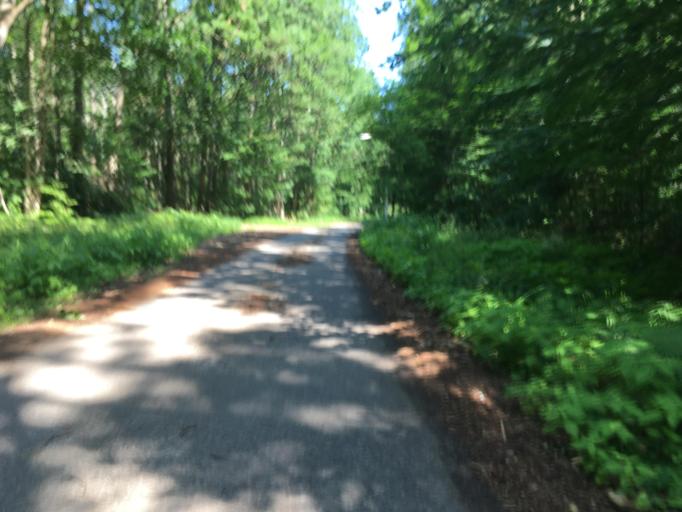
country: DE
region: Brandenburg
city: Marienwerder
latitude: 52.9183
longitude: 13.6631
